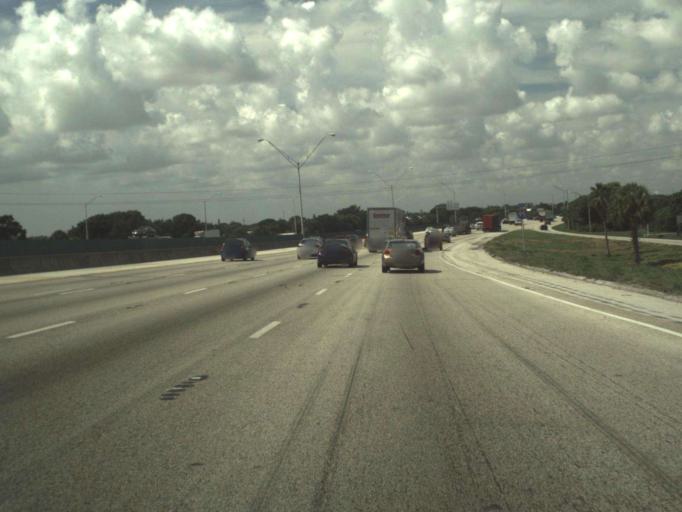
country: US
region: Florida
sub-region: Broward County
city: Tedder
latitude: 26.2733
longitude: -80.1252
